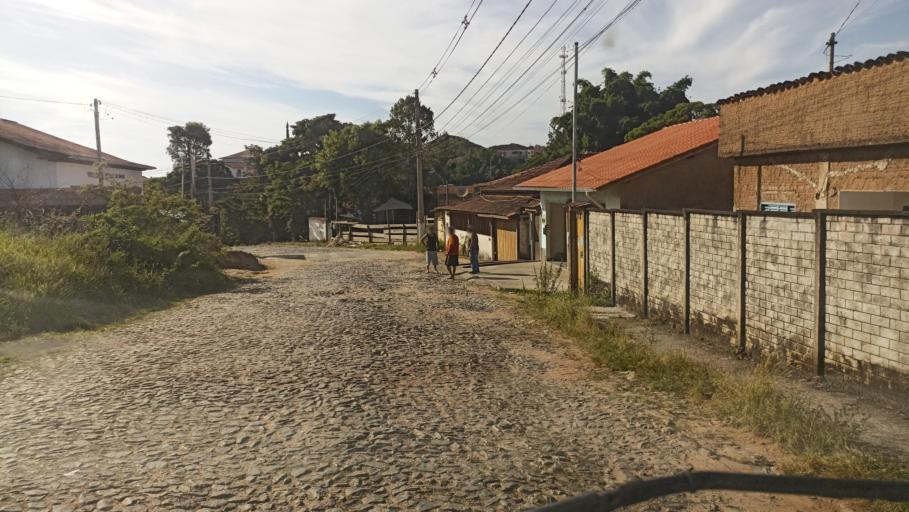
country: BR
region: Minas Gerais
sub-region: Tiradentes
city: Tiradentes
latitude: -21.1144
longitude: -44.1842
